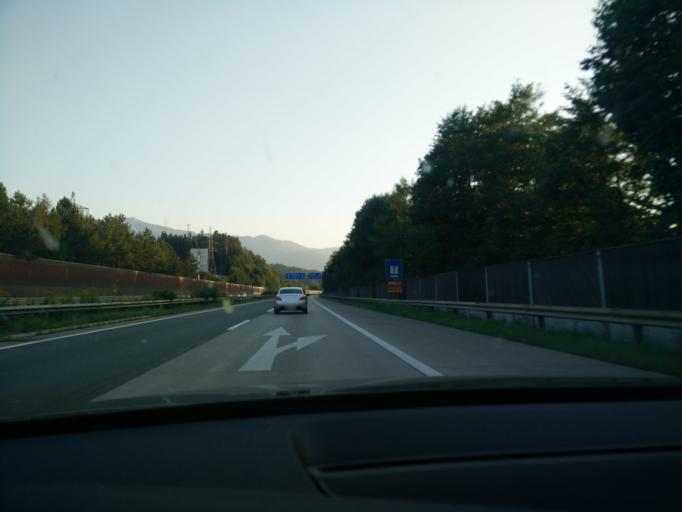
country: AT
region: Carinthia
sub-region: Villach Stadt
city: Villach
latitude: 46.6051
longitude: 13.8895
